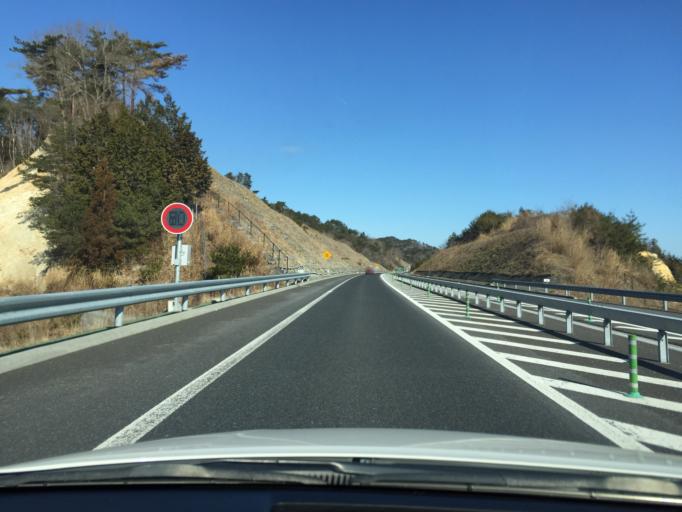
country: JP
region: Fukushima
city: Namie
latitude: 37.6811
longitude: 140.9173
